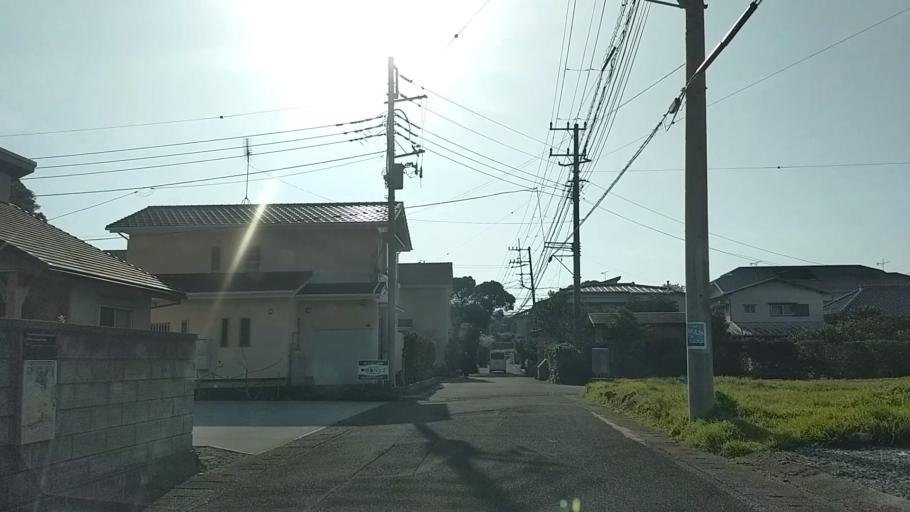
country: JP
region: Shizuoka
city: Shimoda
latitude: 34.7475
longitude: 138.9981
